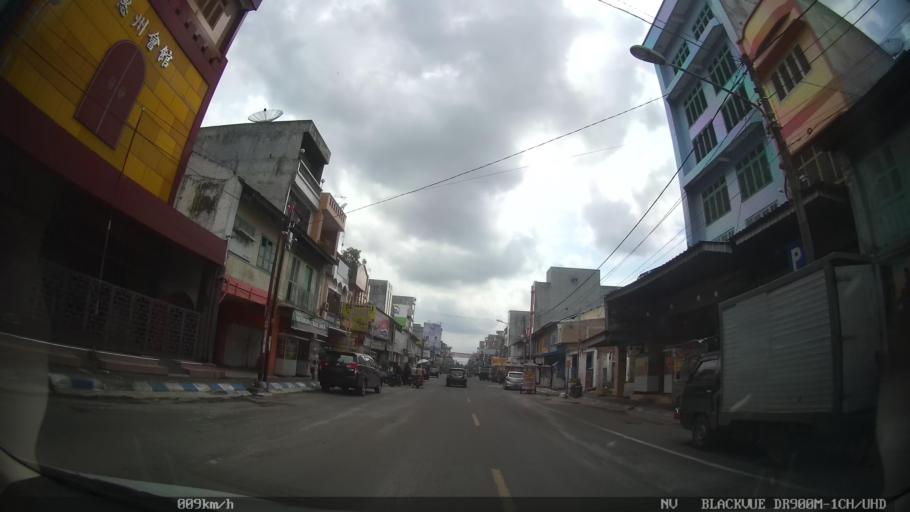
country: ID
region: North Sumatra
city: Percut
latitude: 3.5626
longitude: 98.8777
